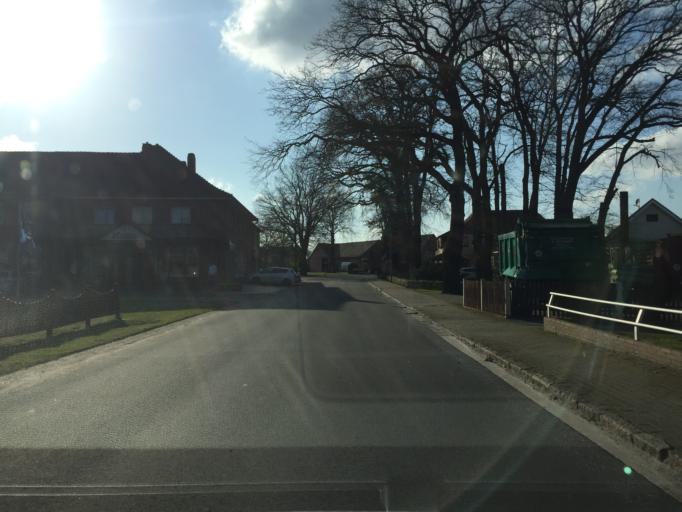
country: DE
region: Lower Saxony
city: Varrel
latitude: 52.6544
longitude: 8.7473
